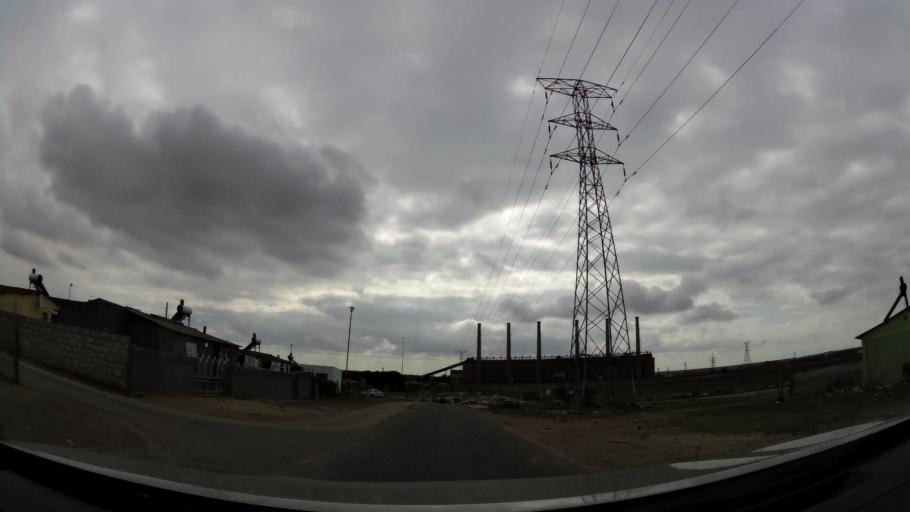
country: ZA
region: Eastern Cape
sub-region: Nelson Mandela Bay Metropolitan Municipality
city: Port Elizabeth
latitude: -33.8759
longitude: 25.5963
